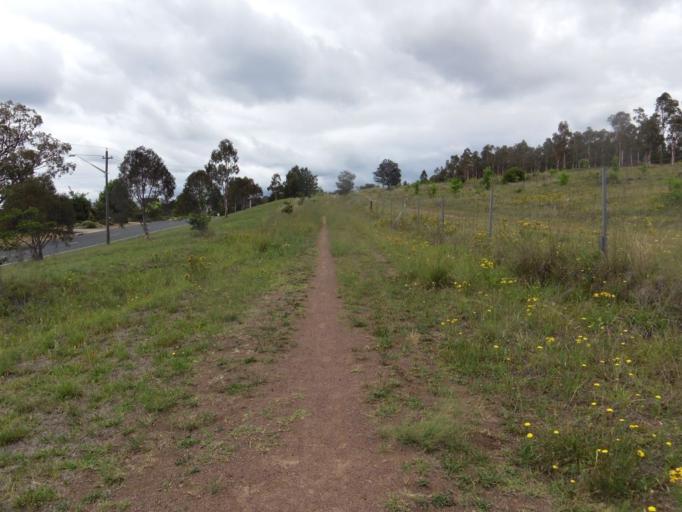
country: AU
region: Australian Capital Territory
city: Macquarie
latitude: -35.3336
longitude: 149.0264
